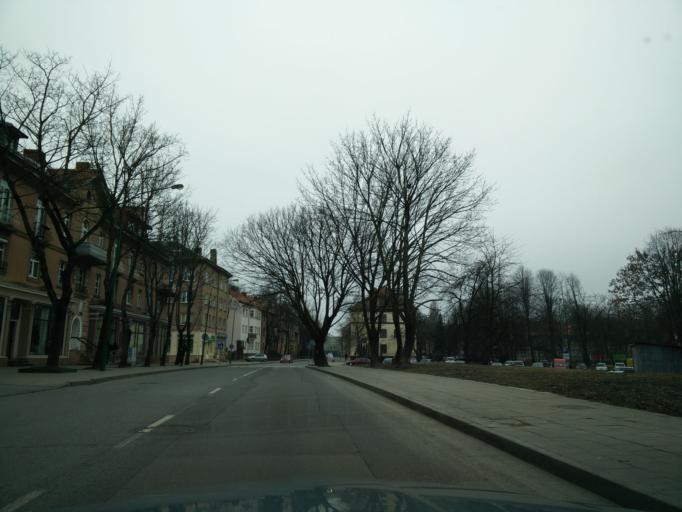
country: LT
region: Klaipedos apskritis
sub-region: Klaipeda
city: Klaipeda
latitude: 55.7057
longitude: 21.1381
